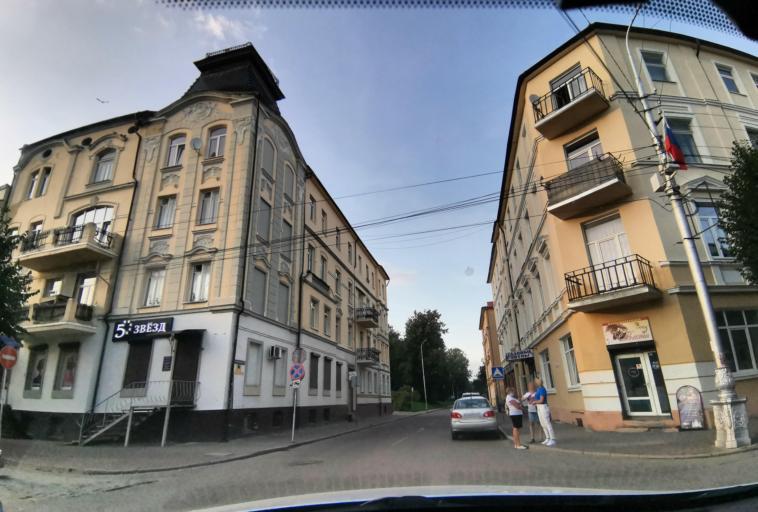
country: RU
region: Kaliningrad
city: Sovetsk
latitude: 55.0811
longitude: 21.8898
